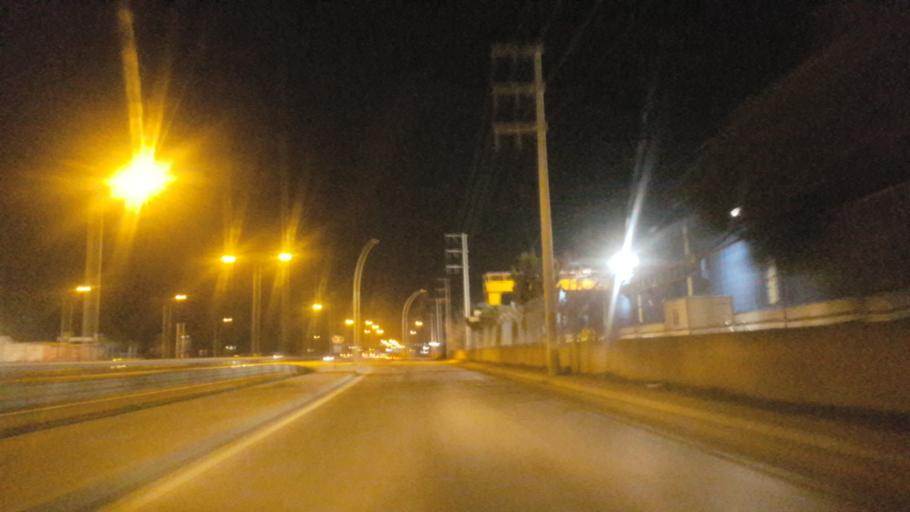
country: TR
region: Kocaeli
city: Gebze
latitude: 40.7987
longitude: 29.4491
